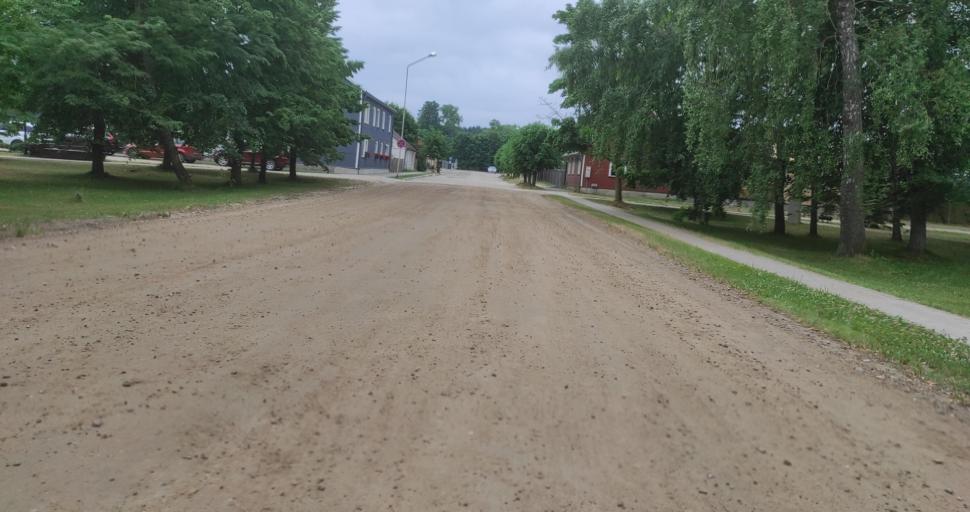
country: LV
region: Pavilostas
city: Pavilosta
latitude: 56.8899
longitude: 21.1795
